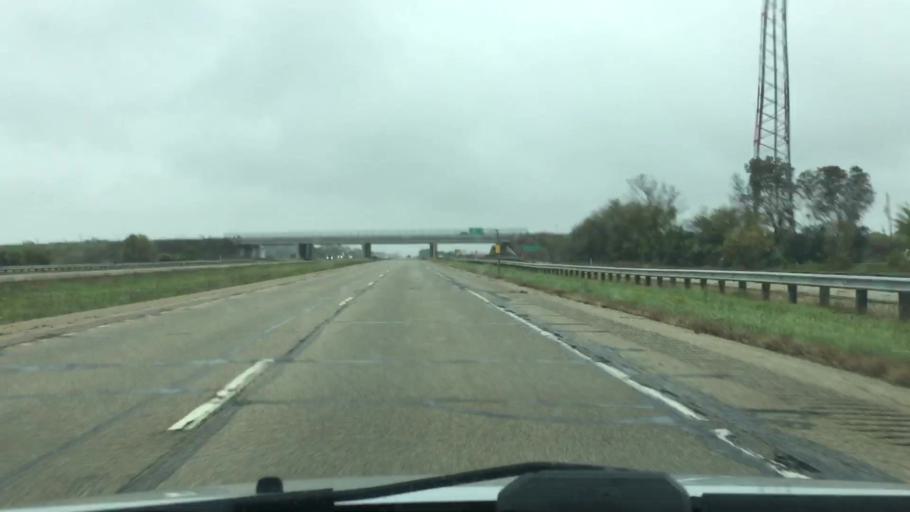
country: US
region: Wisconsin
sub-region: Walworth County
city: Elkhorn
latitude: 42.6722
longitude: -88.5205
